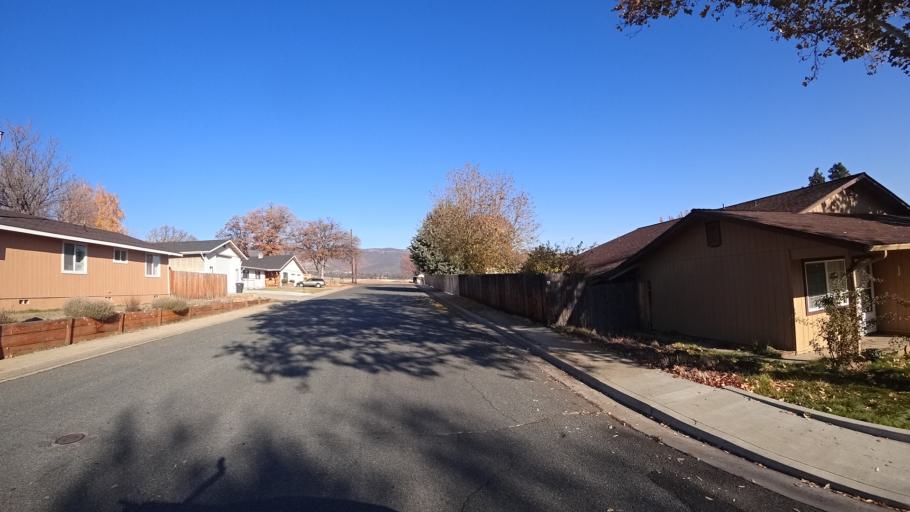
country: US
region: California
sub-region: Siskiyou County
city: Yreka
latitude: 41.7230
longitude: -122.6477
